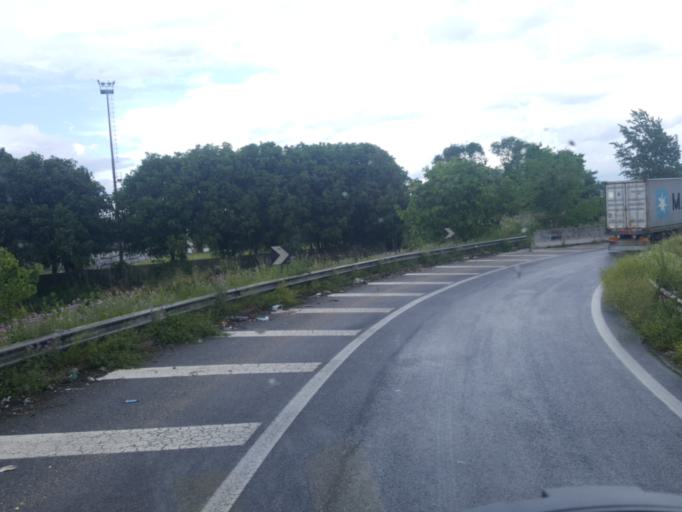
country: IT
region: Campania
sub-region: Provincia di Napoli
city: Pascarola
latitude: 40.9930
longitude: 14.2919
